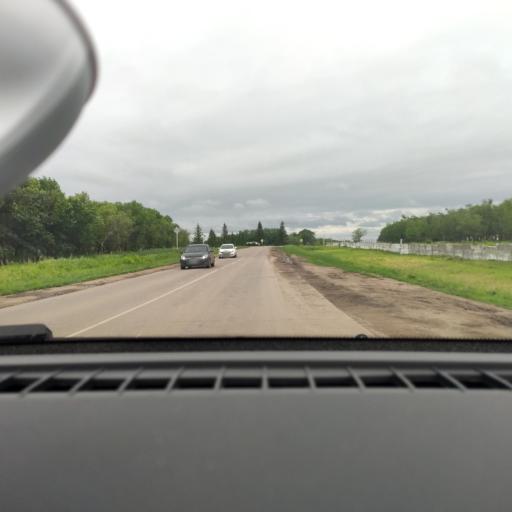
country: RU
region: Samara
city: Spiridonovka
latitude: 53.0556
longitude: 50.4858
